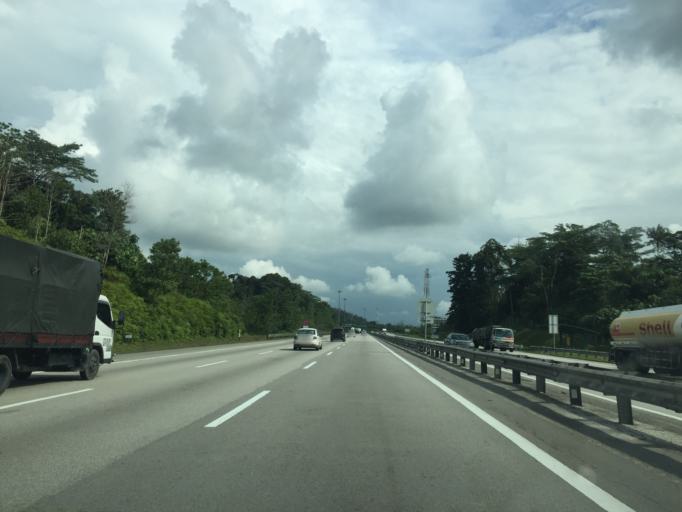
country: MY
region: Selangor
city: Batang Berjuntai
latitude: 3.5702
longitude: 101.5232
